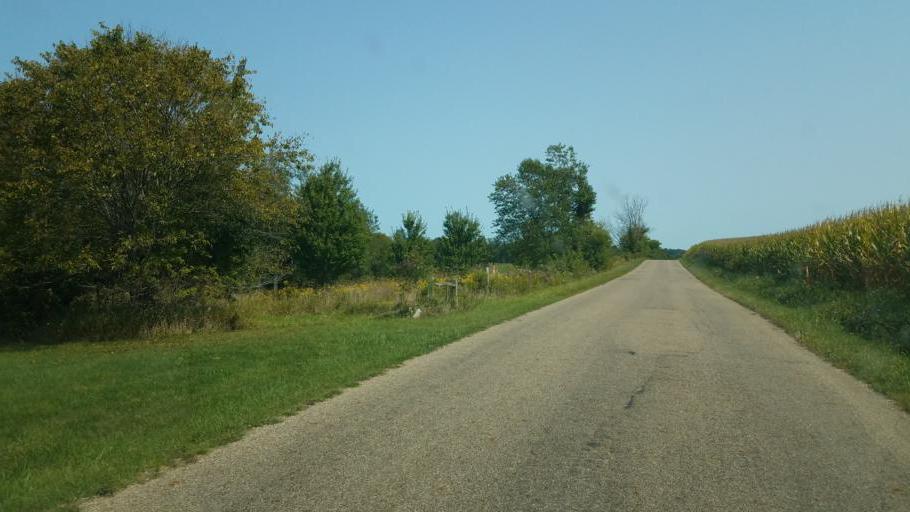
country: US
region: Ohio
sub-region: Knox County
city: Gambier
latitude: 40.4919
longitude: -82.3719
